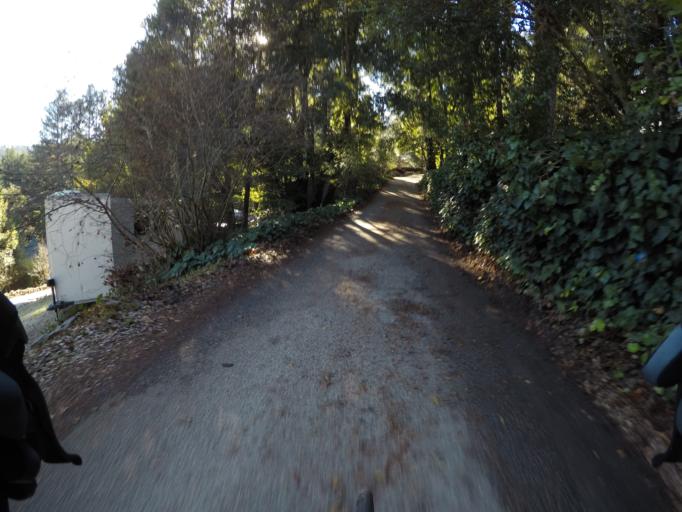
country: US
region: California
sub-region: Santa Cruz County
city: Felton
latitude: 37.0376
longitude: -122.0757
